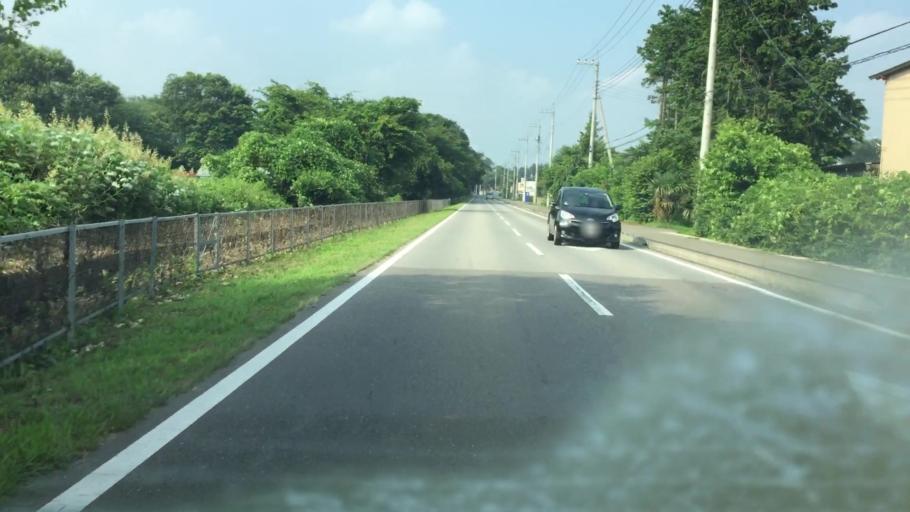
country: JP
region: Tochigi
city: Kuroiso
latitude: 36.9900
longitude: 139.9908
